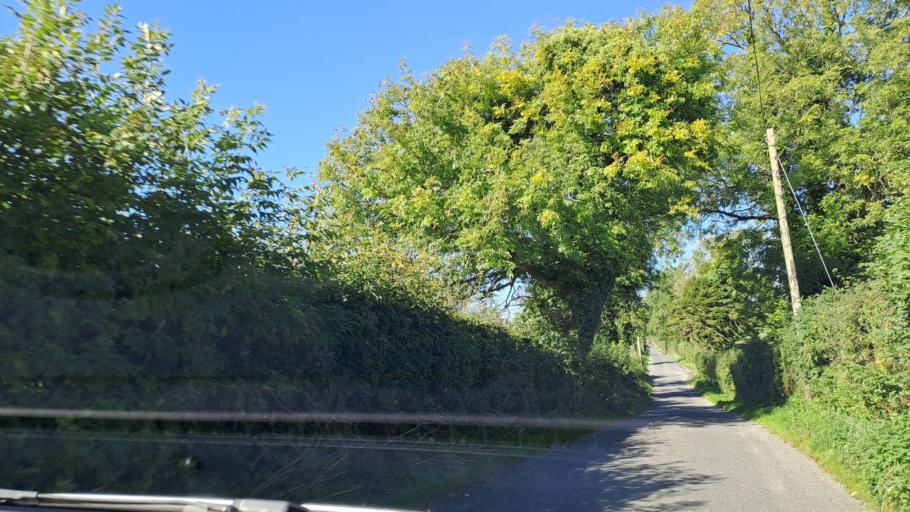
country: IE
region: Ulster
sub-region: County Monaghan
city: Carrickmacross
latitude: 54.0011
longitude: -6.7769
